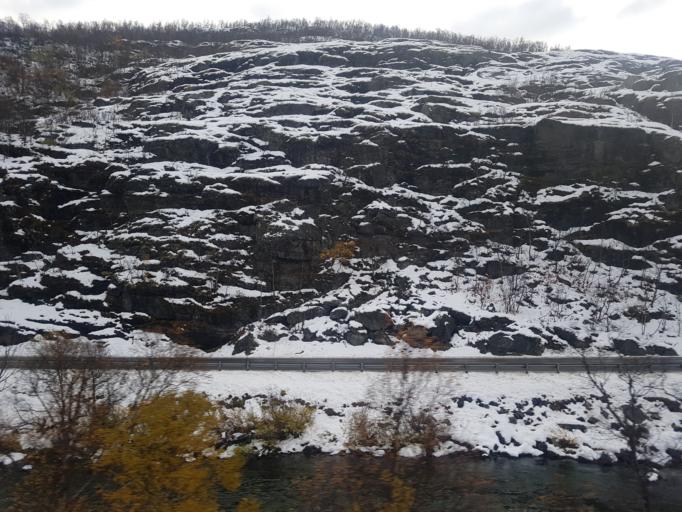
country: NO
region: Sor-Trondelag
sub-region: Oppdal
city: Oppdal
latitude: 62.3320
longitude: 9.6211
